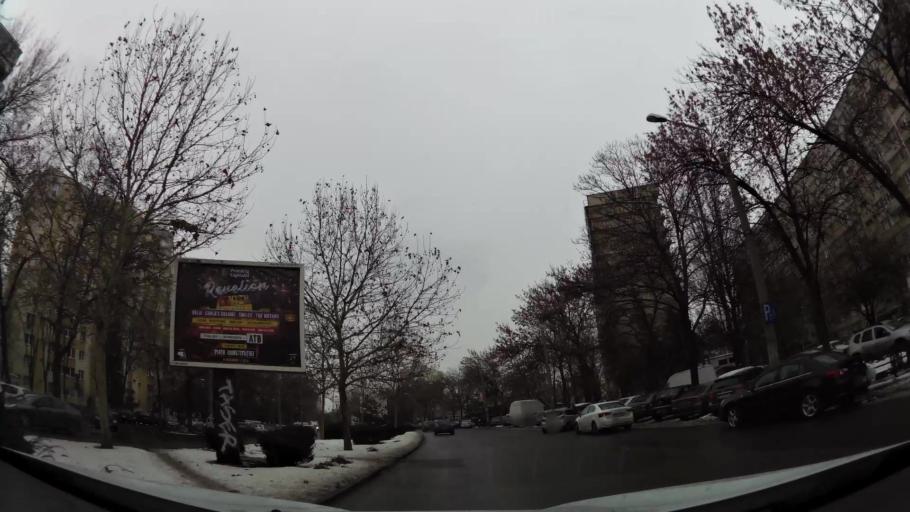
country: RO
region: Ilfov
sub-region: Comuna Chiajna
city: Rosu
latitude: 44.4163
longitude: 26.0257
